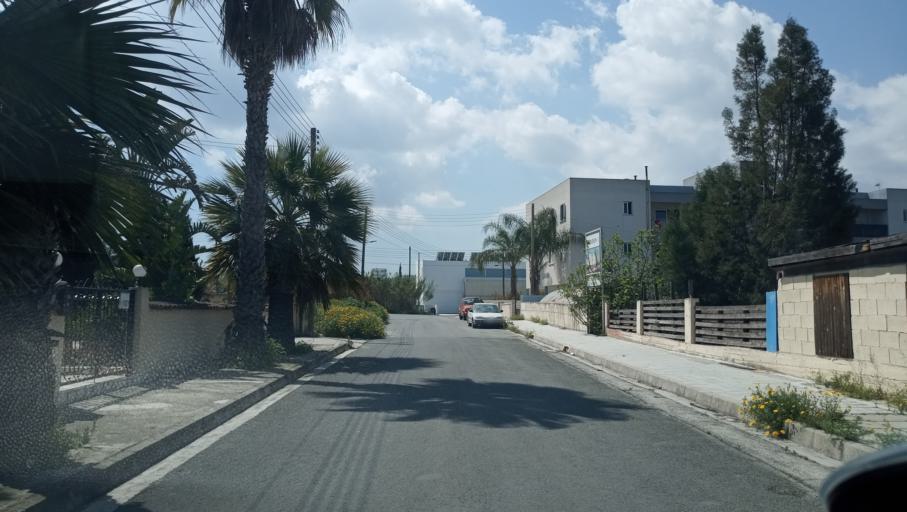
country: CY
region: Lefkosia
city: Dali
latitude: 35.0174
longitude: 33.4154
